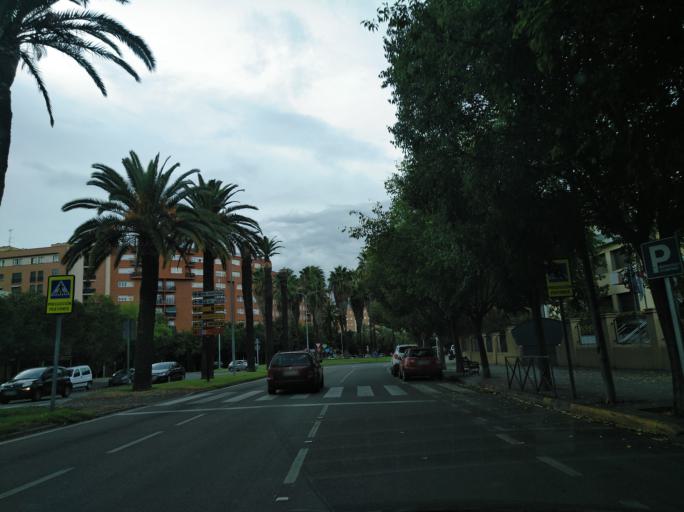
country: ES
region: Extremadura
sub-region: Provincia de Badajoz
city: Badajoz
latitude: 38.8665
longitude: -6.9852
